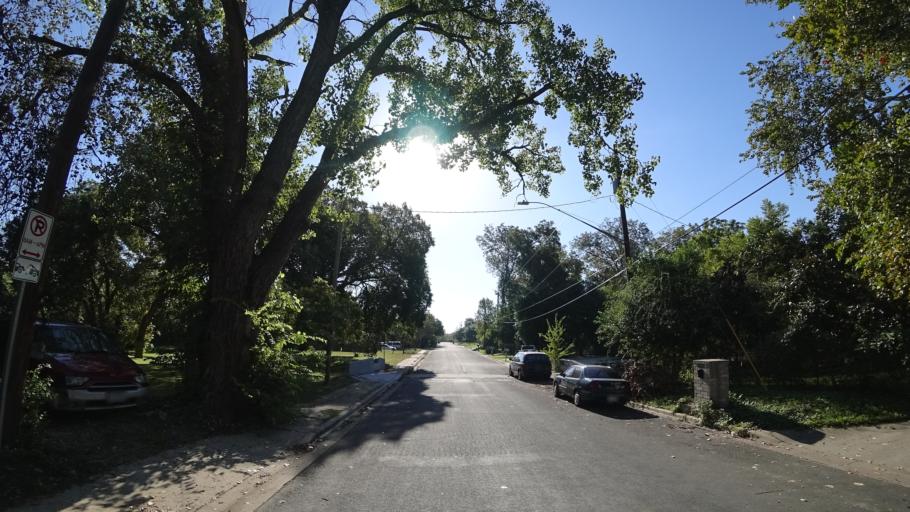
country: US
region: Texas
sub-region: Travis County
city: Wells Branch
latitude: 30.3547
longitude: -97.7021
